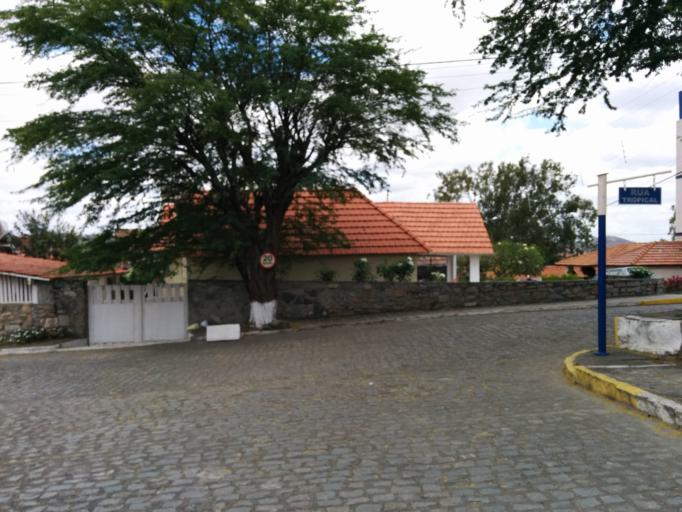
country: BR
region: Pernambuco
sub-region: Gravata
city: Gravata
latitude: -8.1941
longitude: -35.5615
